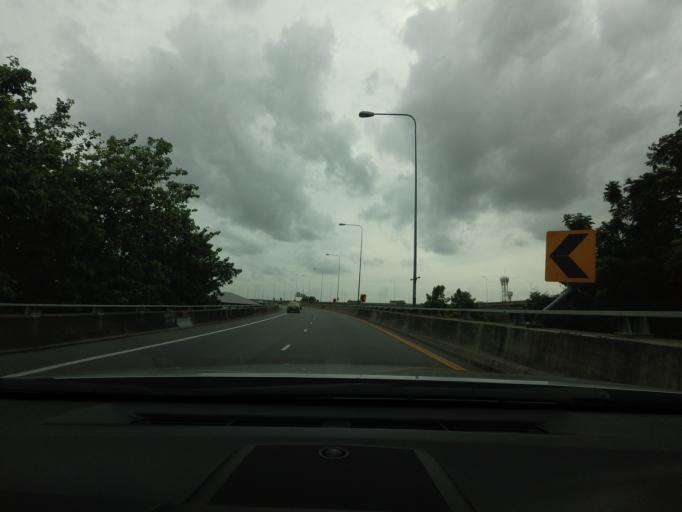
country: TH
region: Bangkok
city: Ratchathewi
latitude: 13.7713
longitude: 100.5318
